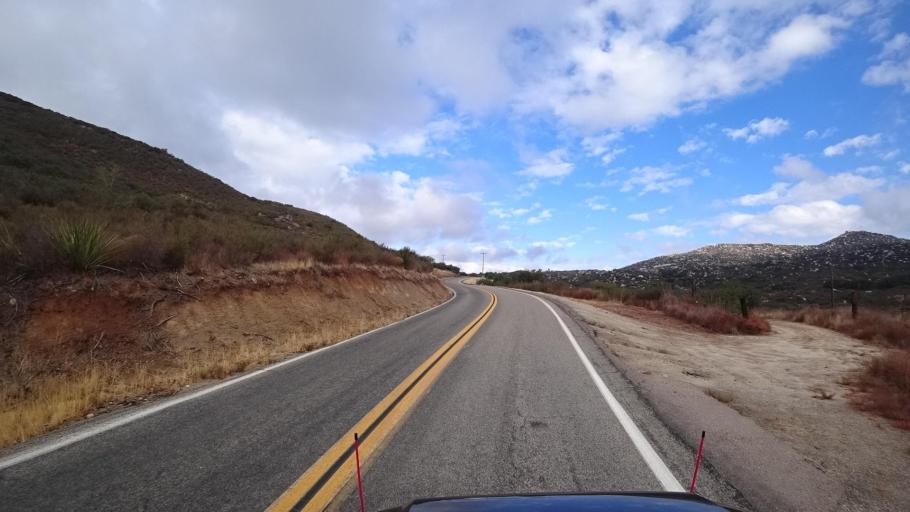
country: MX
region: Baja California
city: Tecate
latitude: 32.6242
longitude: -116.6235
